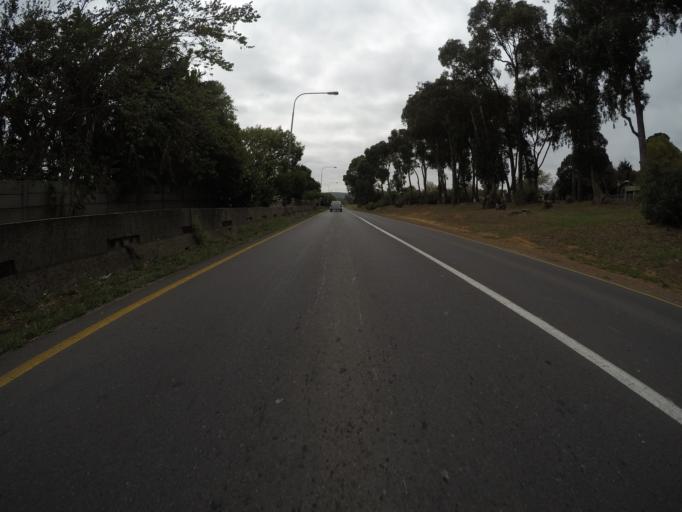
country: ZA
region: Western Cape
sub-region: City of Cape Town
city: Kraaifontein
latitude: -33.8539
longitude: 18.6315
